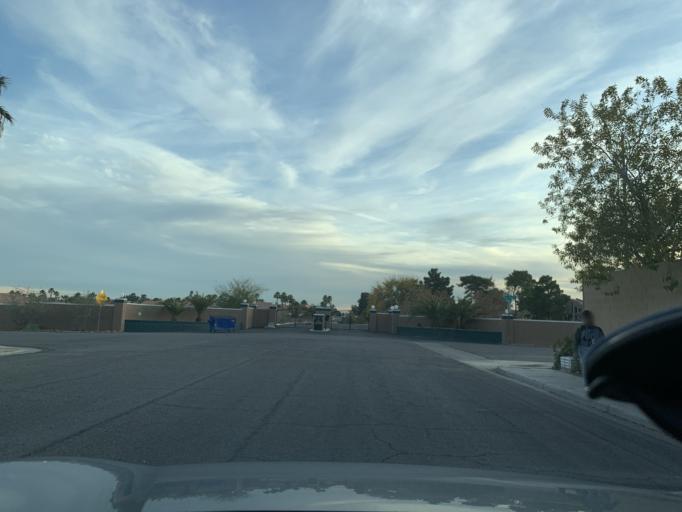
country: US
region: Nevada
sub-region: Clark County
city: Spring Valley
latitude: 36.0910
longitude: -115.2296
